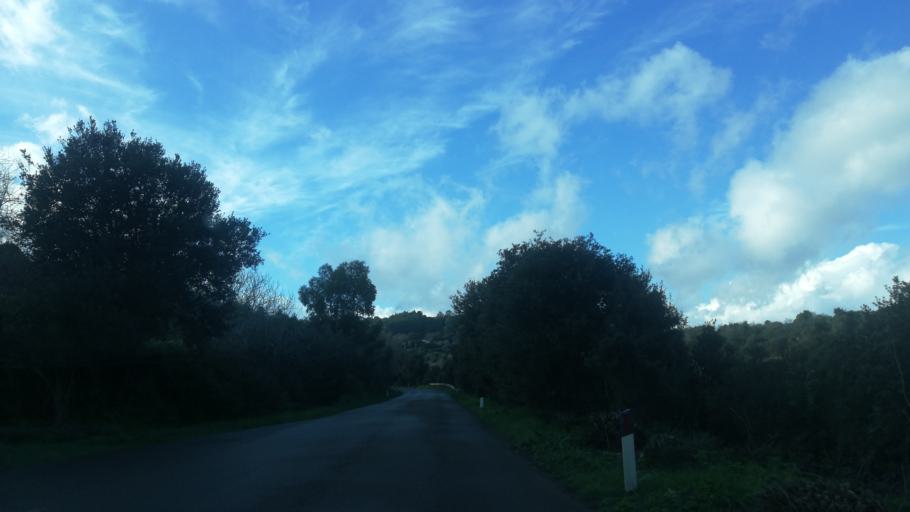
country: IT
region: Sardinia
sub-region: Provincia di Medio Campidano
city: Villanovaforru
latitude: 39.6334
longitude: 8.8626
